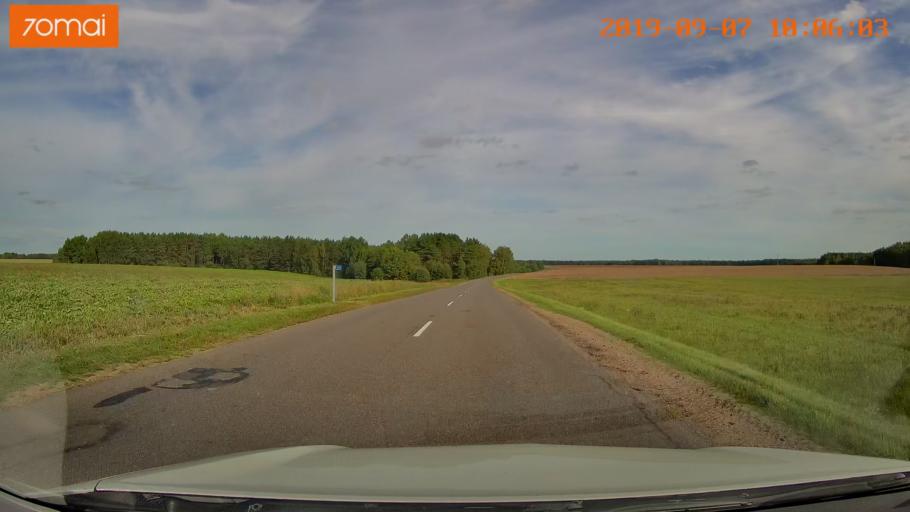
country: BY
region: Grodnenskaya
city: Voranava
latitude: 54.0560
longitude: 25.4041
